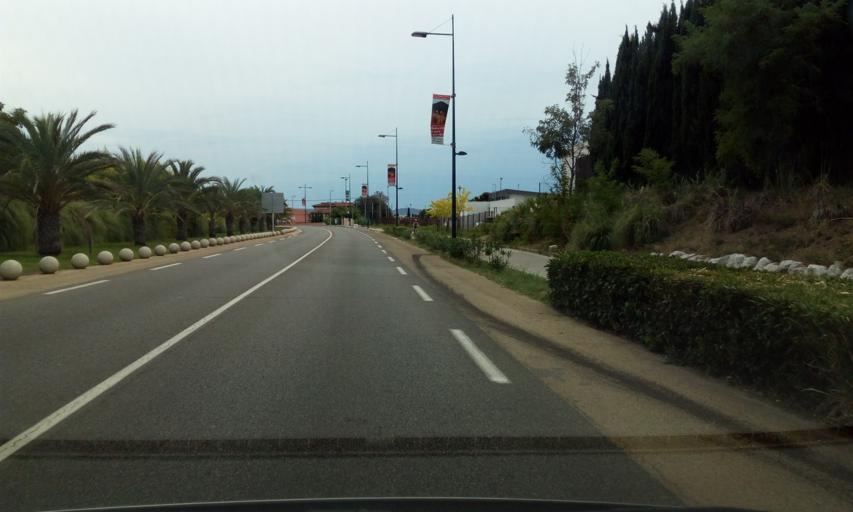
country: FR
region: Provence-Alpes-Cote d'Azur
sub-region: Departement du Var
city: Carqueiranne
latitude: 43.0947
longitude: 6.0706
